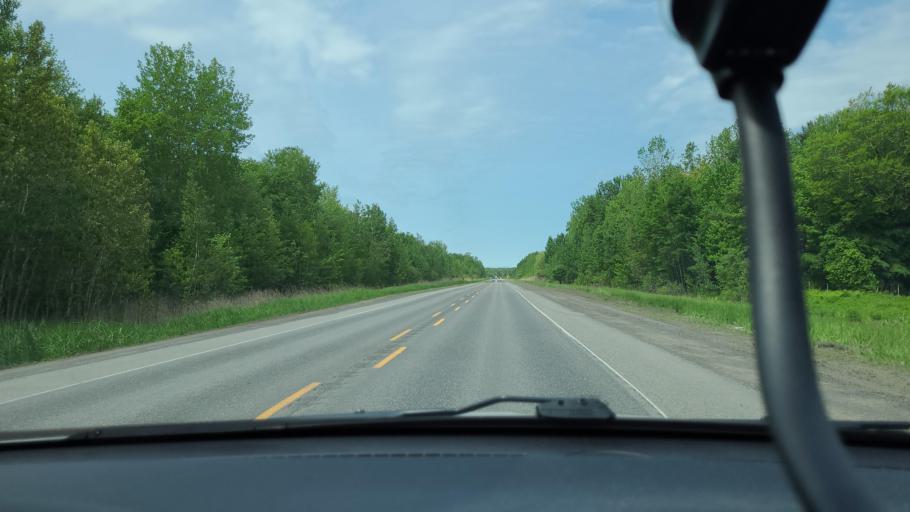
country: CA
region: Quebec
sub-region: Lanaudiere
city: Saint-Jacques
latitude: 45.9672
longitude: -73.5265
